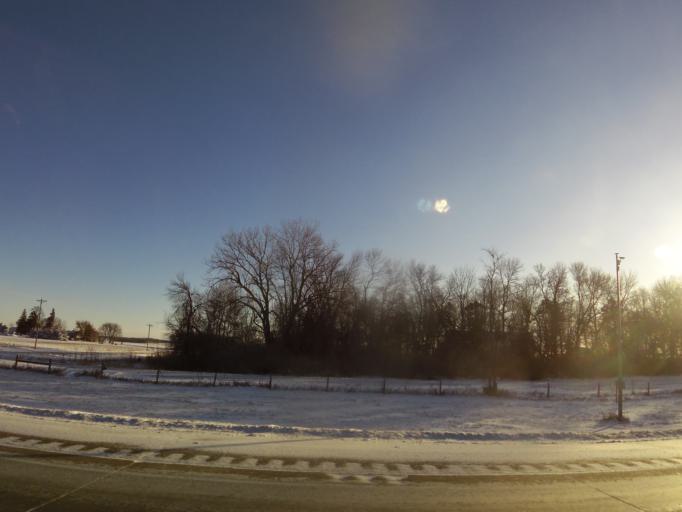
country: US
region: Minnesota
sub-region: Steele County
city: Owatonna
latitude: 43.9203
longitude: -93.2768
